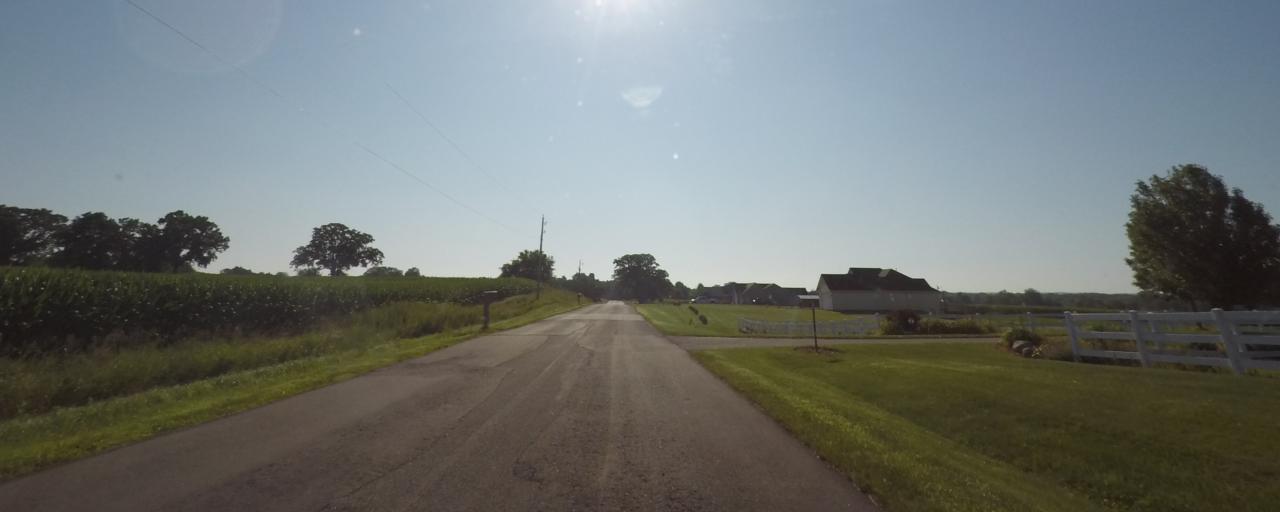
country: US
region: Wisconsin
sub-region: Jefferson County
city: Palmyra
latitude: 42.9152
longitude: -88.5690
